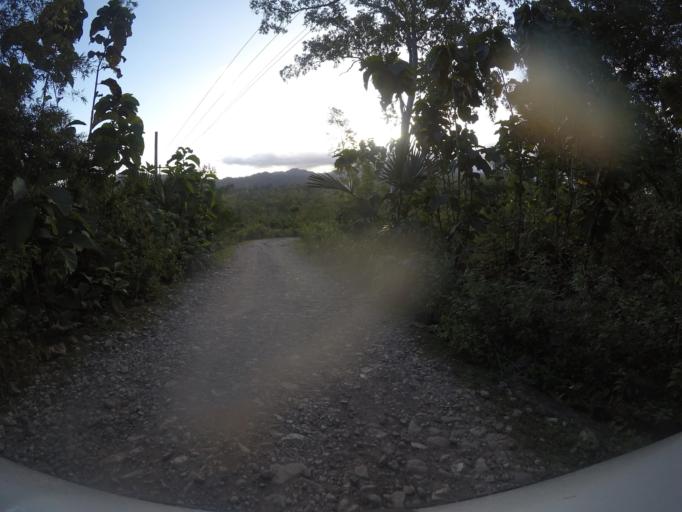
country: TL
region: Baucau
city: Venilale
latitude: -8.7211
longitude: 126.7111
